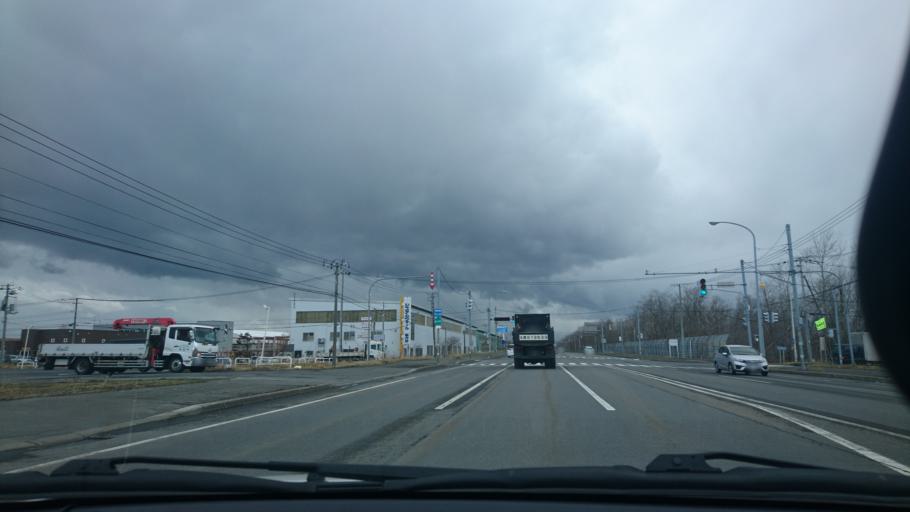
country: JP
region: Hokkaido
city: Ishikari
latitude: 43.1942
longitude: 141.3276
